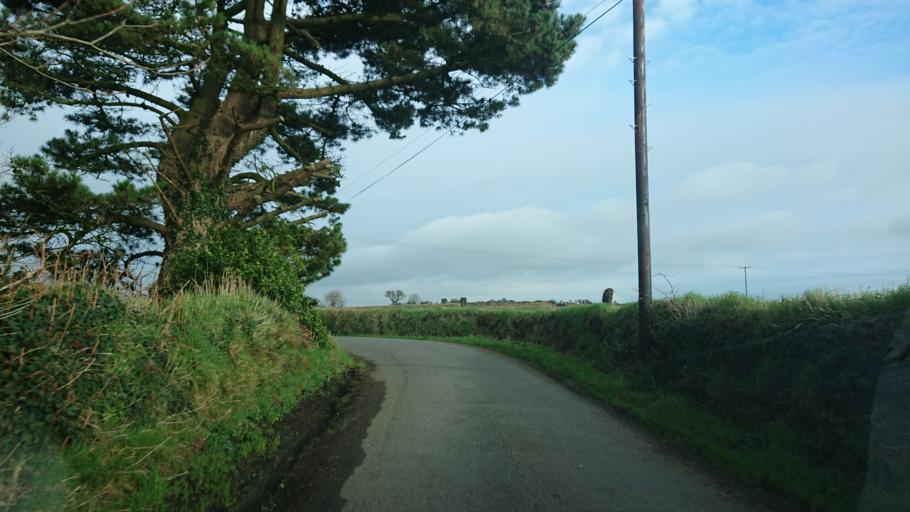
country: IE
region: Munster
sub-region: Waterford
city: Tra Mhor
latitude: 52.1560
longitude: -7.2148
